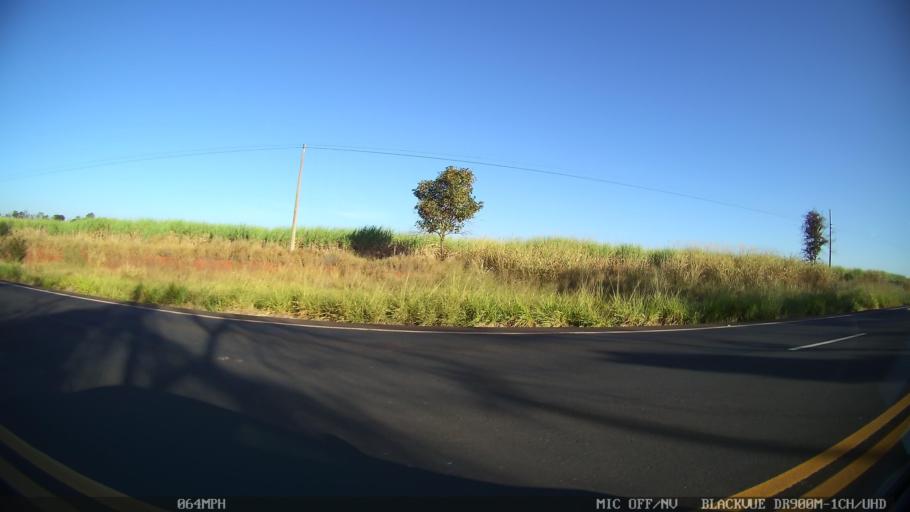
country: BR
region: Sao Paulo
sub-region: Olimpia
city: Olimpia
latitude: -20.7295
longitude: -49.0509
